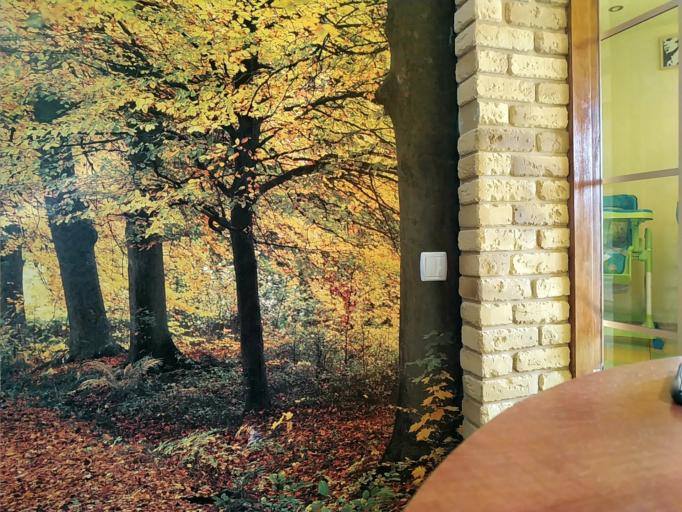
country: RU
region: Novgorod
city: Parfino
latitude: 57.8018
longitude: 31.6071
